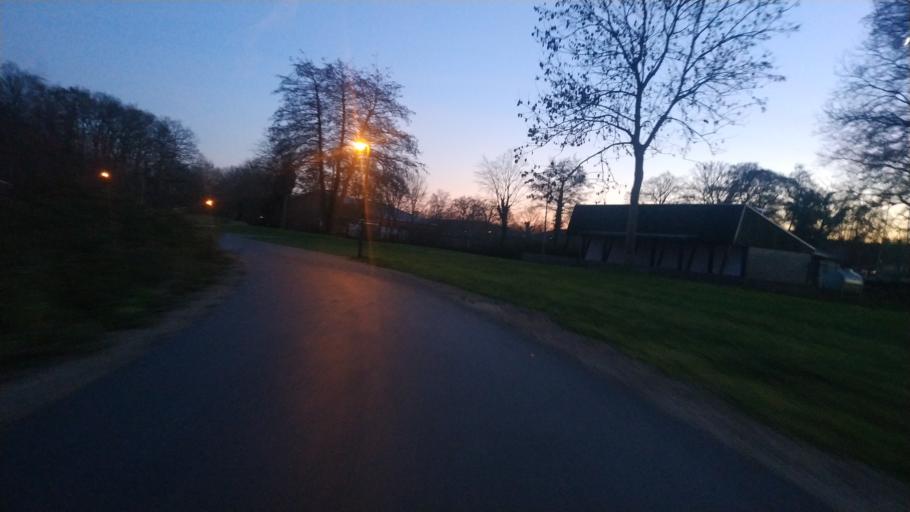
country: DE
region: North Rhine-Westphalia
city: Ibbenburen
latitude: 52.2655
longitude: 7.7273
